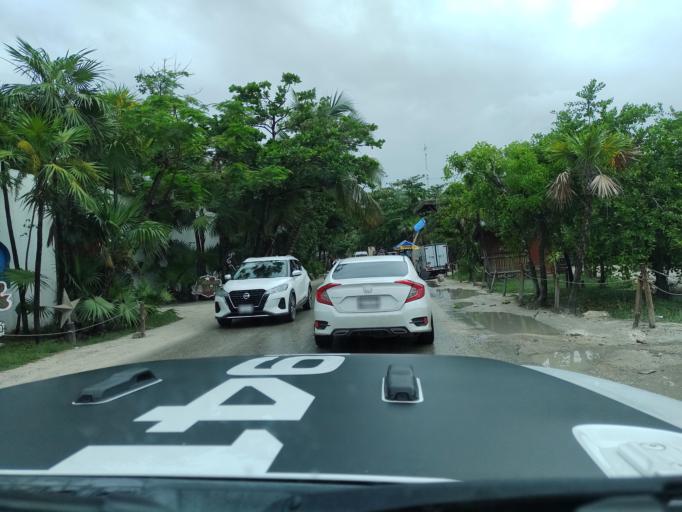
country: MX
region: Quintana Roo
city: Tulum
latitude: 20.1586
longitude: -87.4558
